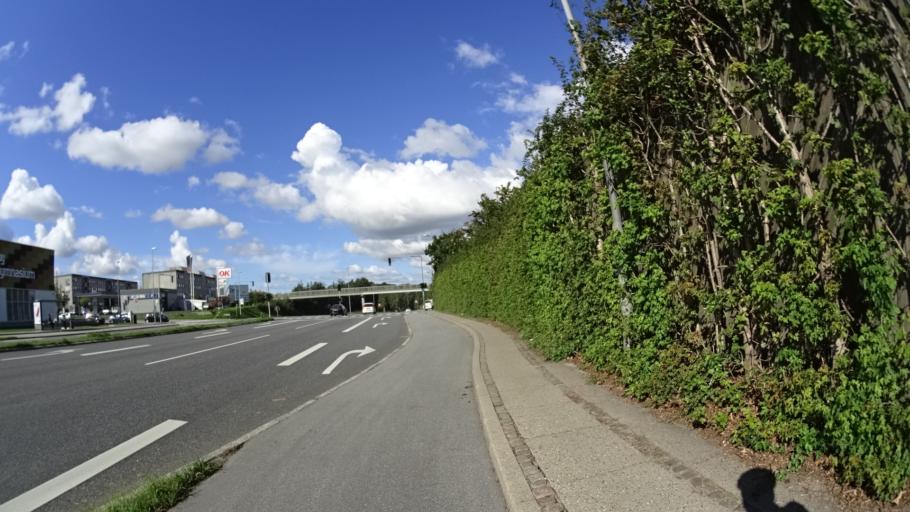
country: DK
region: Central Jutland
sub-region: Arhus Kommune
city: Stavtrup
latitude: 56.1139
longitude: 10.1539
